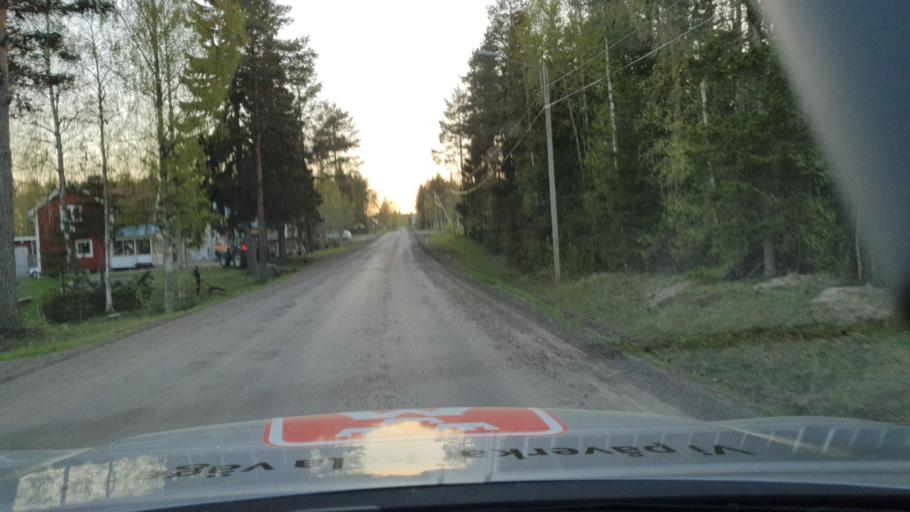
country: SE
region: Vaesternorrland
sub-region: OErnskoeldsviks Kommun
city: Ornskoldsvik
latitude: 63.5267
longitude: 18.5391
